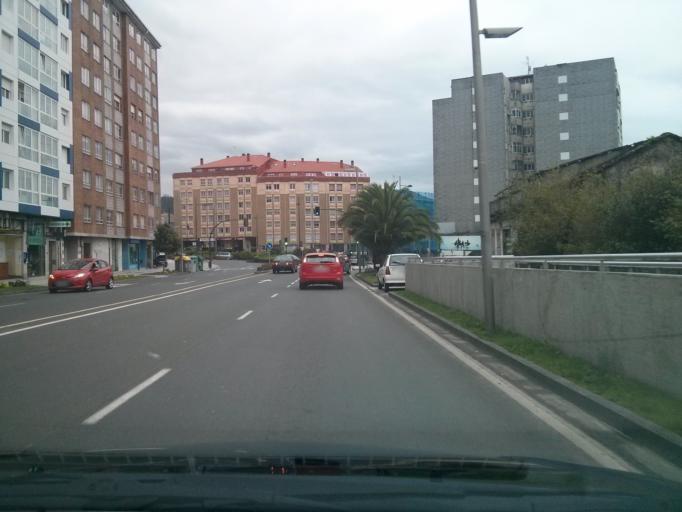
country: ES
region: Galicia
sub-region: Provincia da Coruna
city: Santiago de Compostela
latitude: 42.8703
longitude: -8.5494
